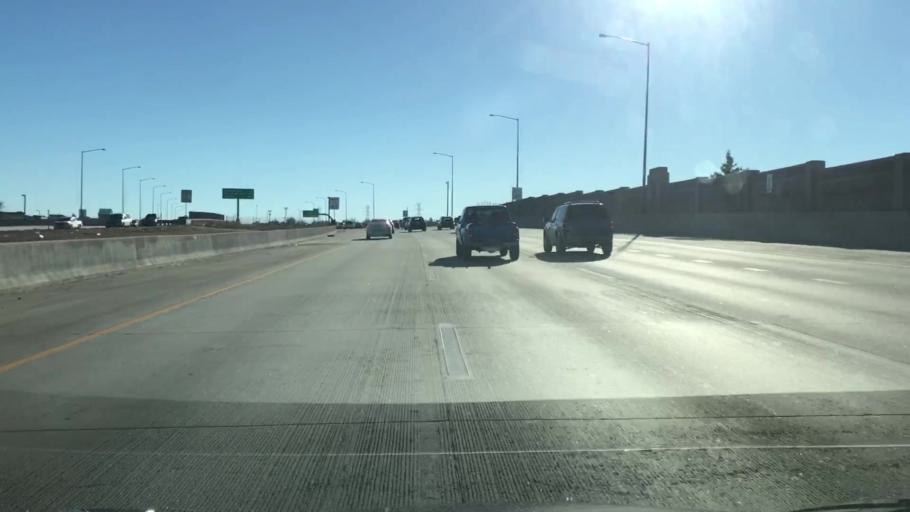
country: US
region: Colorado
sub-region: Adams County
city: Aurora
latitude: 39.7197
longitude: -104.8268
